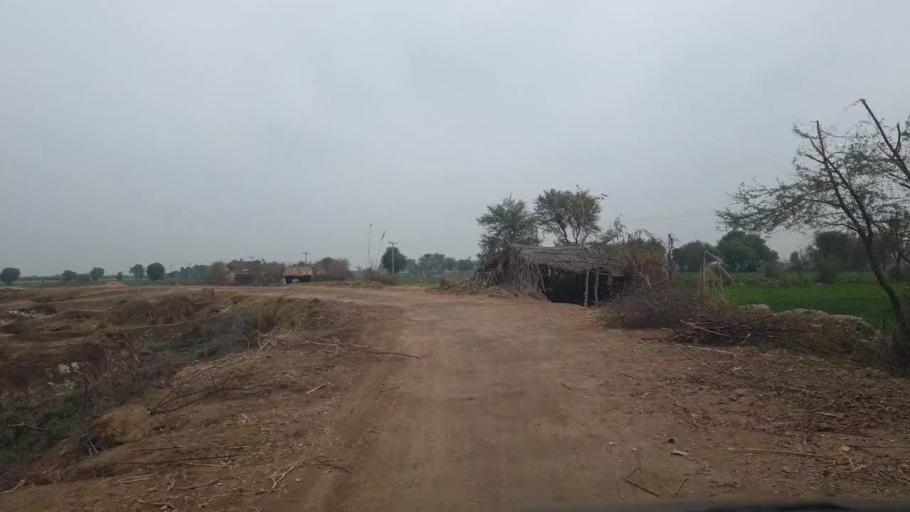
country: PK
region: Sindh
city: Tando Adam
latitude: 25.8542
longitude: 68.7027
